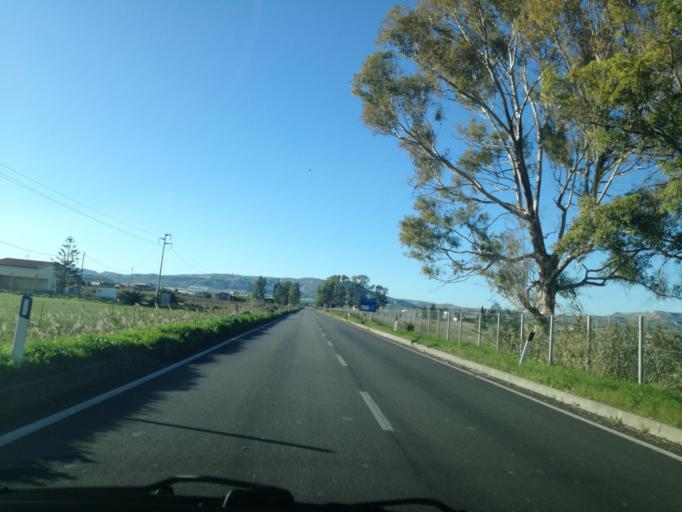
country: IT
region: Sicily
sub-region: Provincia di Caltanissetta
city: Butera
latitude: 37.1183
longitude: 14.1369
